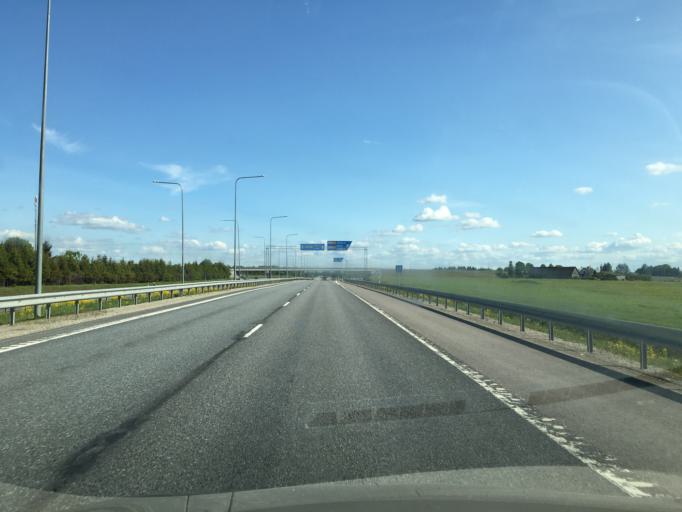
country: EE
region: Harju
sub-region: Rae vald
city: Vaida
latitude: 59.2546
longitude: 25.0106
